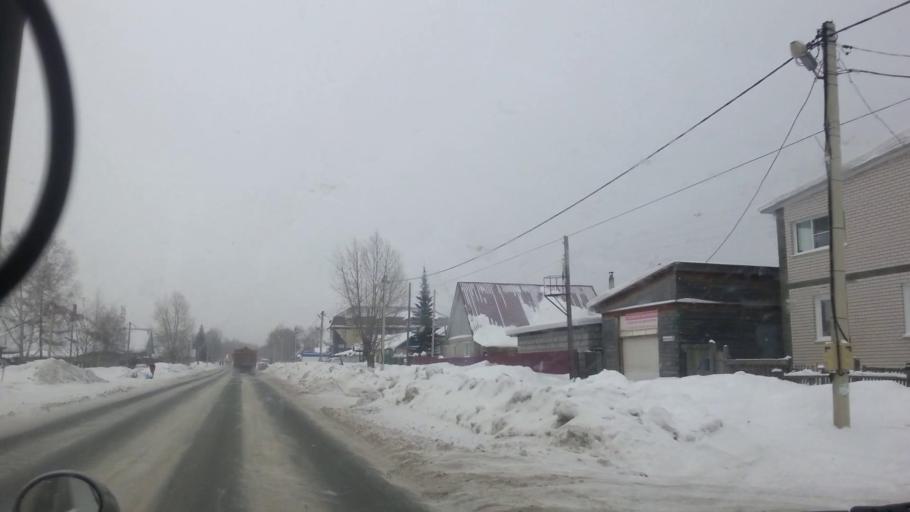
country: RU
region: Altai Krai
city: Vlasikha
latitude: 53.2978
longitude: 83.5860
